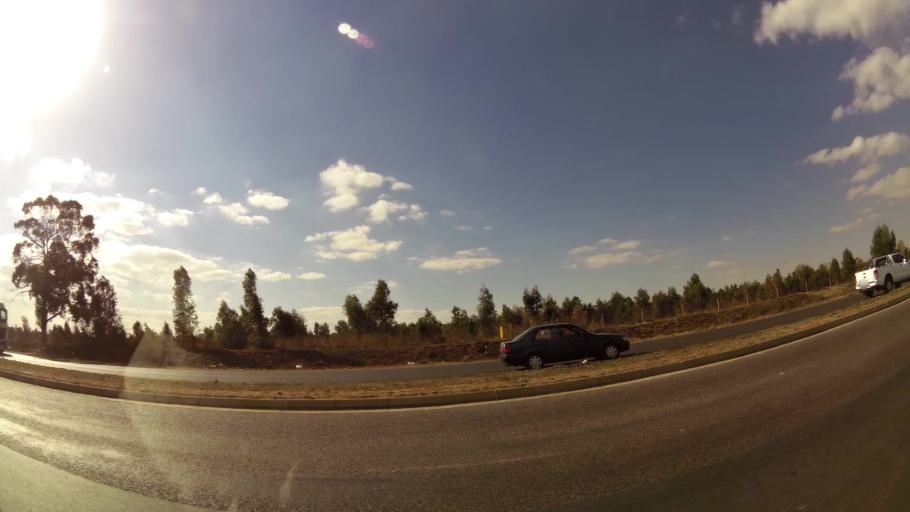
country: ZA
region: Gauteng
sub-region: Ekurhuleni Metropolitan Municipality
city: Tembisa
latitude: -25.9741
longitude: 28.2469
